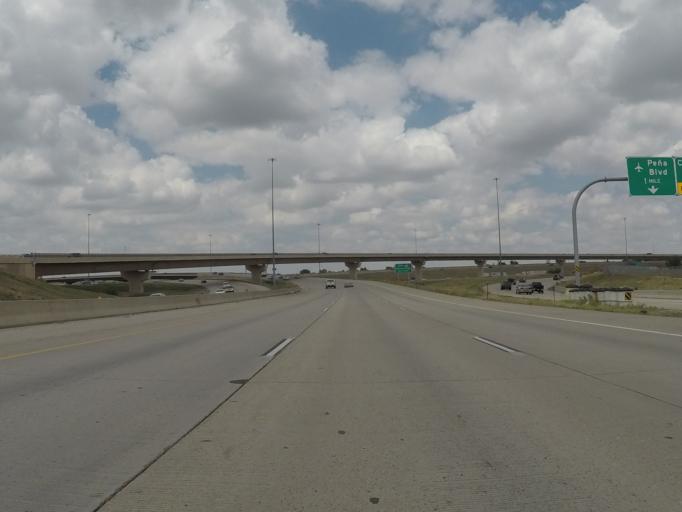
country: US
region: Colorado
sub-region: Adams County
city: Aurora
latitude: 39.7681
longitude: -104.8276
